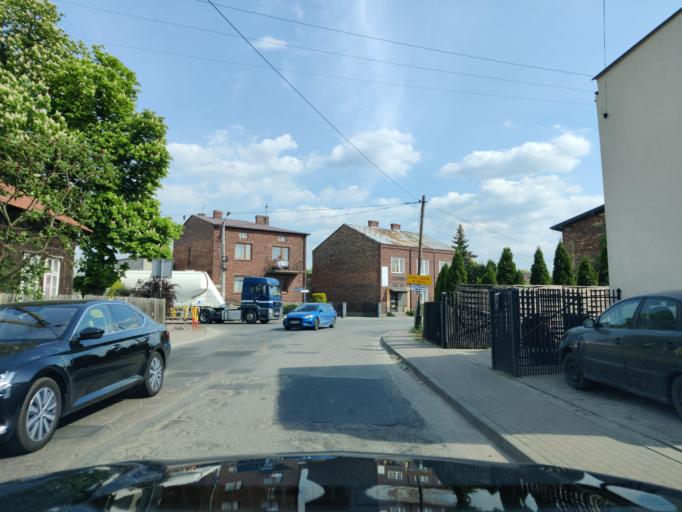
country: PL
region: Silesian Voivodeship
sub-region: Powiat bedzinski
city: Siewierz
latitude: 50.3961
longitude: 19.2412
